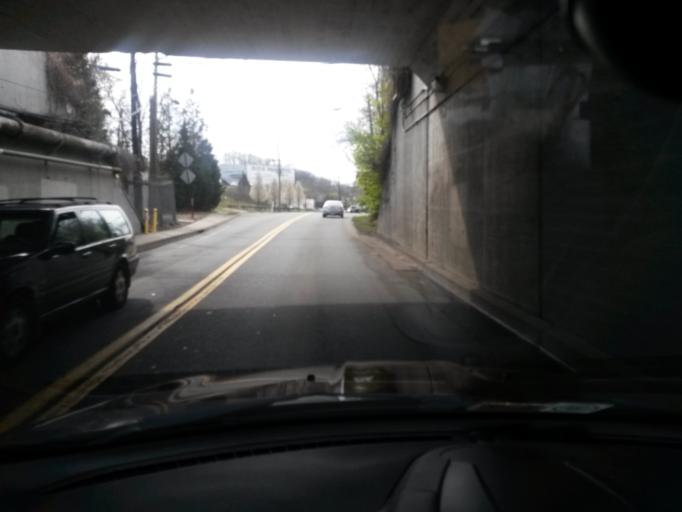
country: US
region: Virginia
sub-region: City of Roanoke
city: Roanoke
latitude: 37.2785
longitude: -79.9769
